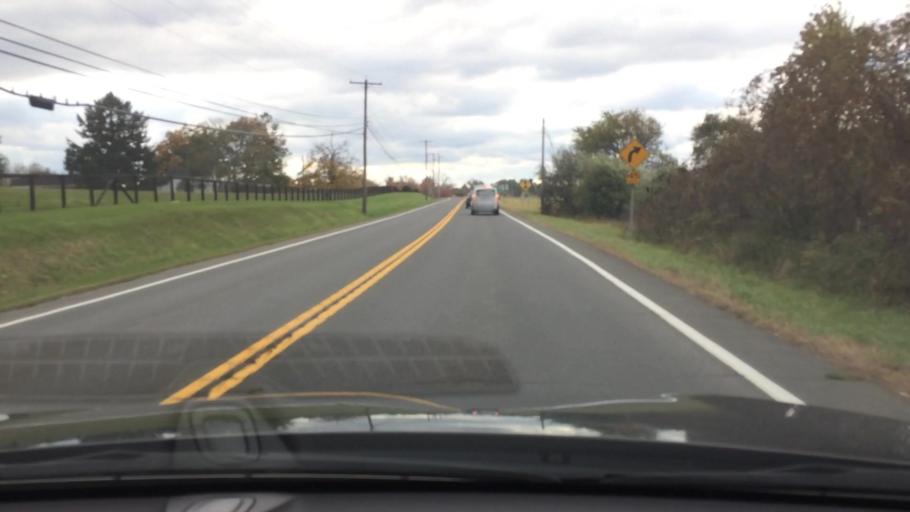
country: US
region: New York
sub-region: Columbia County
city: Oakdale
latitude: 42.1813
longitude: -73.7574
